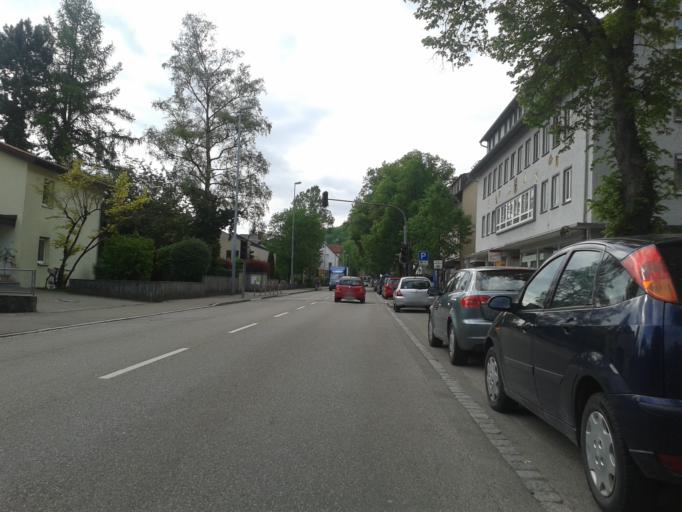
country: DE
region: Baden-Wuerttemberg
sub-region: Tuebingen Region
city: Blaubeuren
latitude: 48.4078
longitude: 9.7878
